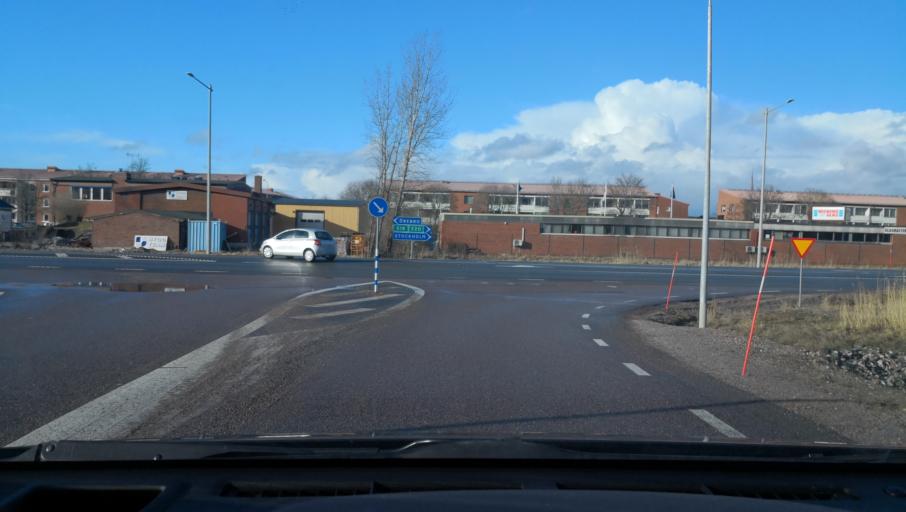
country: SE
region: Vaestmanland
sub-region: Arboga Kommun
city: Arboga
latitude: 59.3885
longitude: 15.8386
